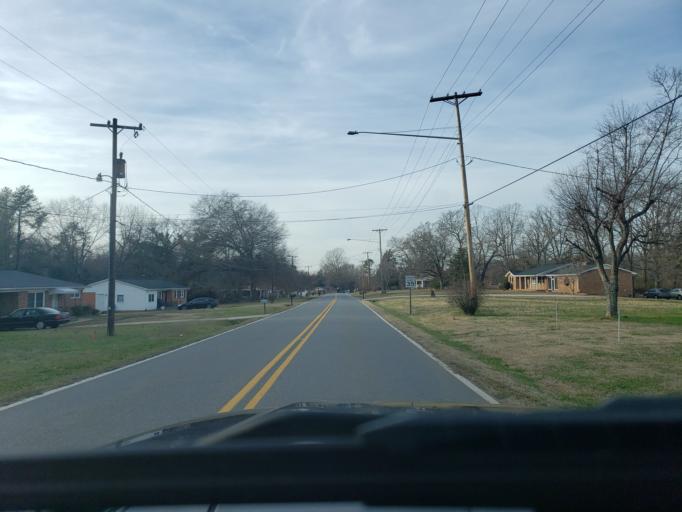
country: US
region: North Carolina
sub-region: Cleveland County
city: Shelby
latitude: 35.2754
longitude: -81.5044
